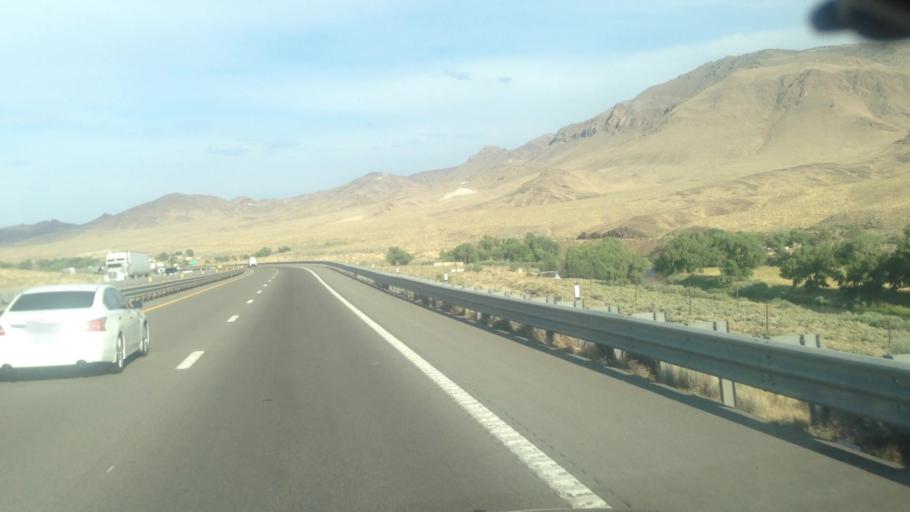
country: US
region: Nevada
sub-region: Lyon County
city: Fernley
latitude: 39.5898
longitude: -119.4017
